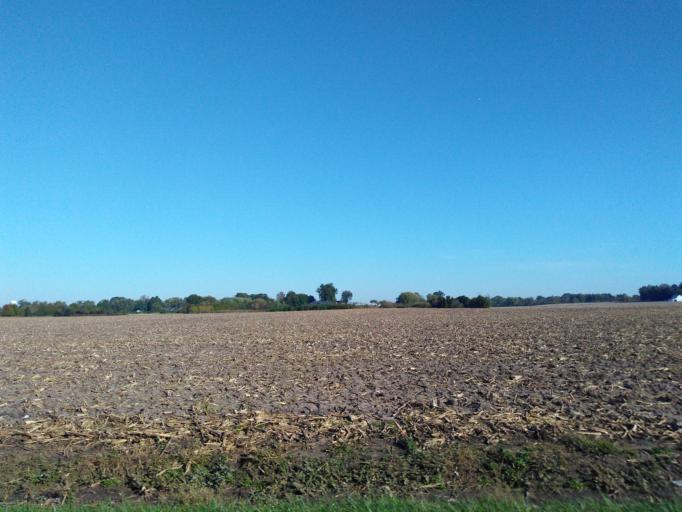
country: US
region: Illinois
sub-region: Madison County
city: Troy
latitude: 38.7176
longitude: -89.8959
